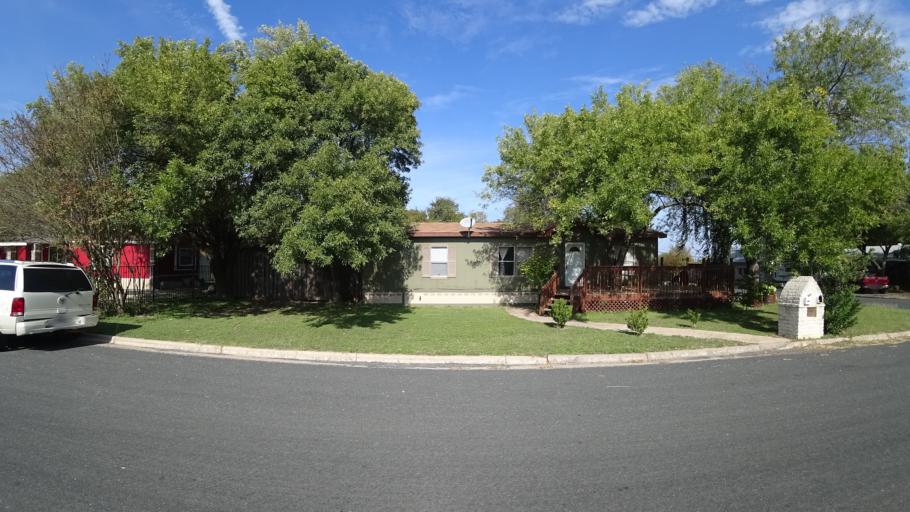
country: US
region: Texas
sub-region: Travis County
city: Pflugerville
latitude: 30.4113
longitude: -97.6290
